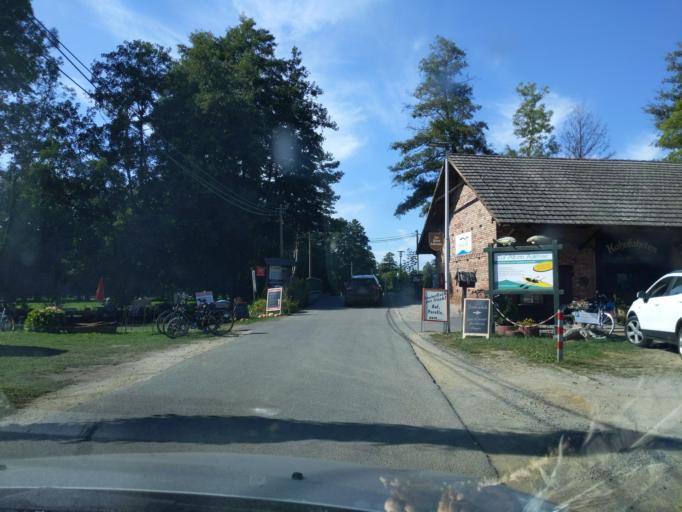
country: DE
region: Brandenburg
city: Straupitz
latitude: 51.8620
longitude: 14.0940
